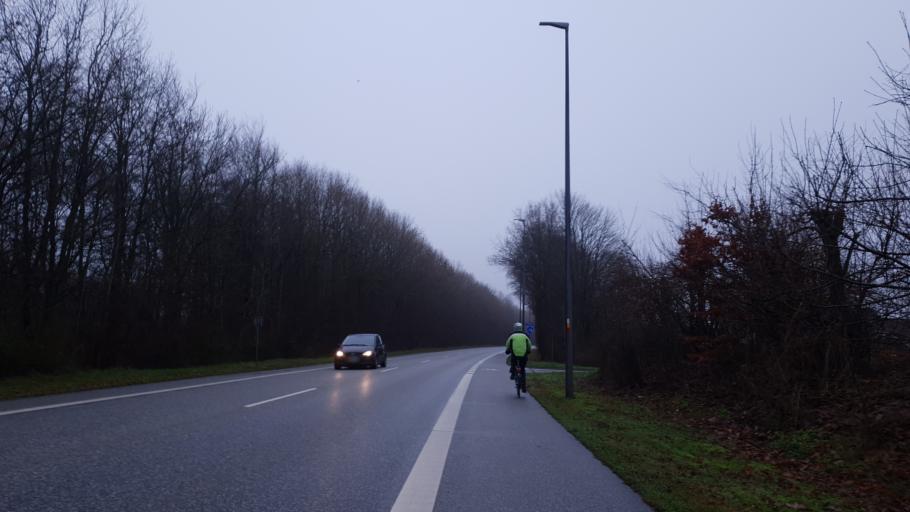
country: DK
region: Central Jutland
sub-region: Hedensted Kommune
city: Hedensted
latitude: 55.7866
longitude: 9.6994
